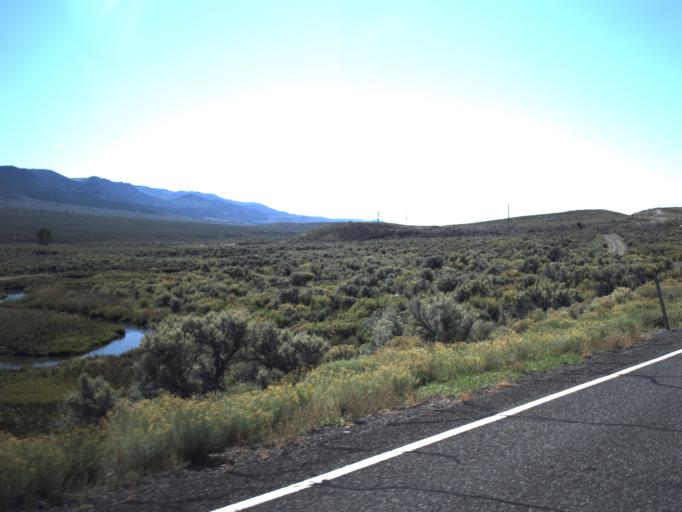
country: US
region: Utah
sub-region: Piute County
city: Junction
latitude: 38.3512
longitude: -111.9497
